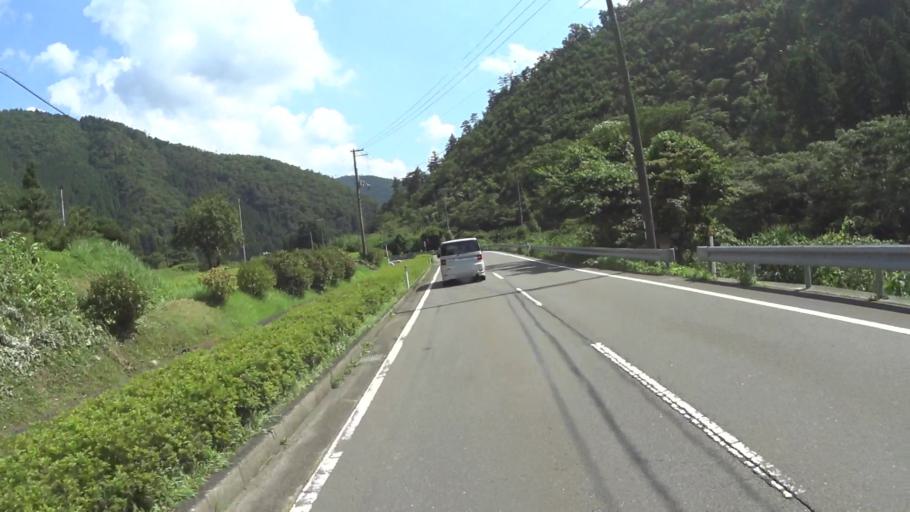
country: JP
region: Kyoto
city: Maizuru
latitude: 35.3060
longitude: 135.5557
